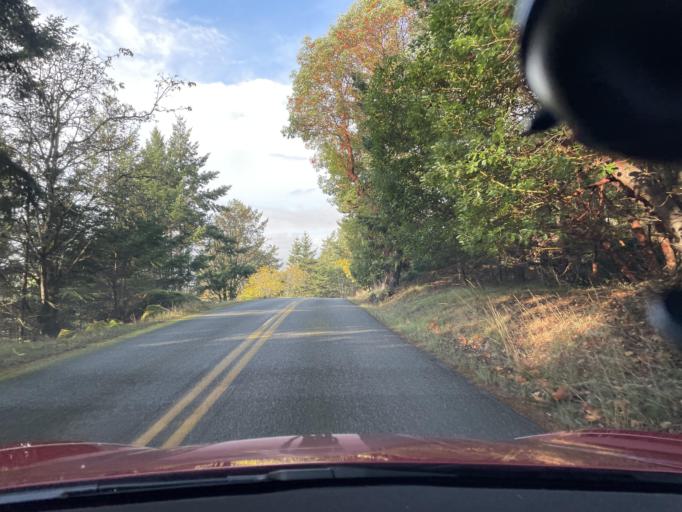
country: US
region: Washington
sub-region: San Juan County
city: Friday Harbor
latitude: 48.5147
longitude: -123.1457
